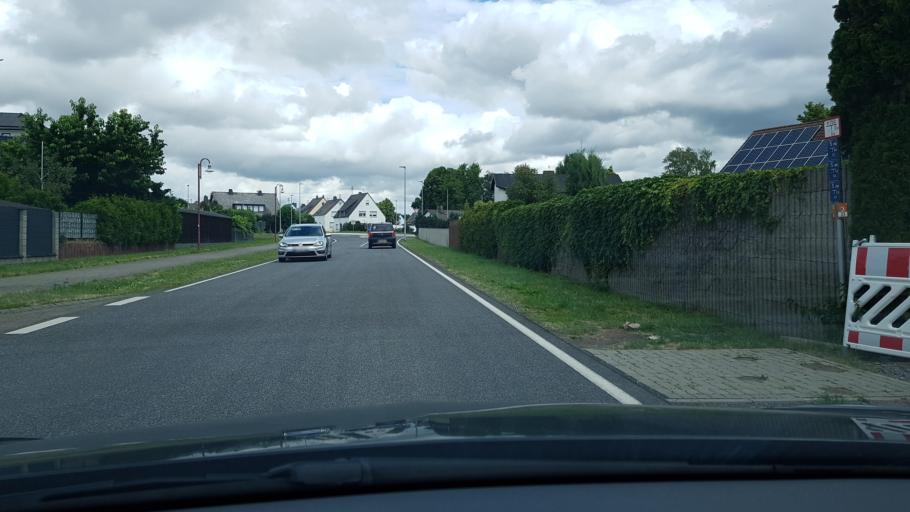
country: DE
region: Rheinland-Pfalz
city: Polch
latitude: 50.2942
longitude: 7.3086
